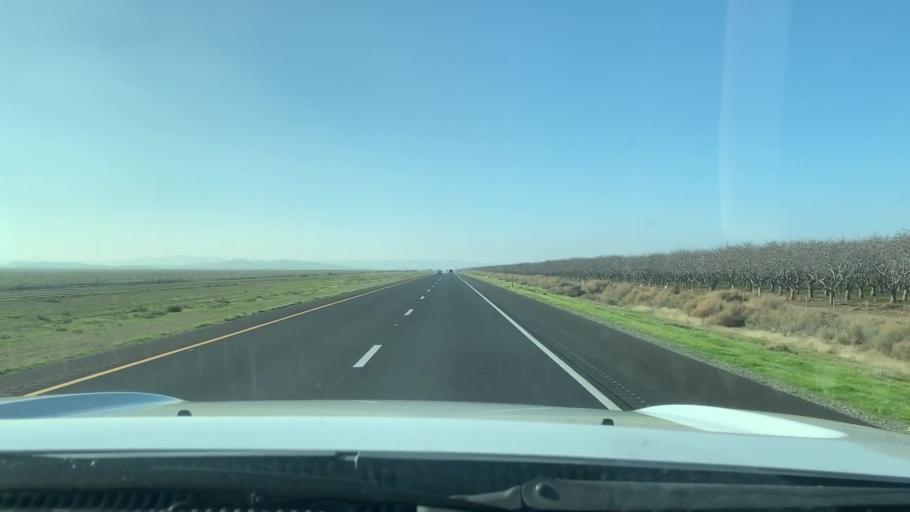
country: US
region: California
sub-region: Kern County
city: Lost Hills
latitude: 35.6148
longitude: -119.9114
